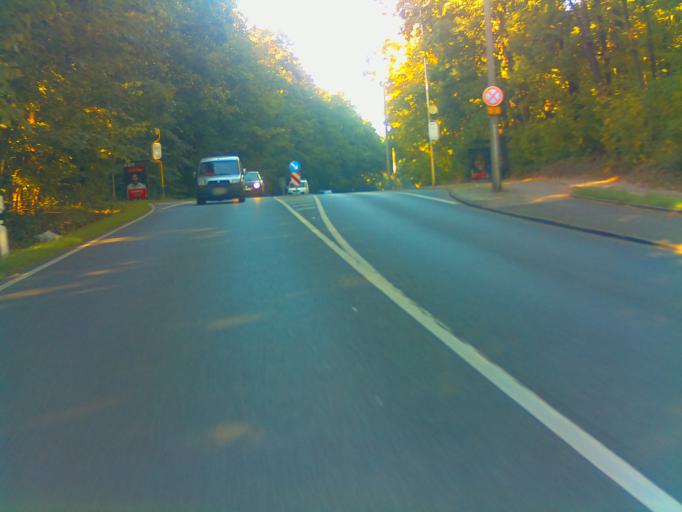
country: DE
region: Thuringia
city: Gera
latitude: 50.8664
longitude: 12.0528
